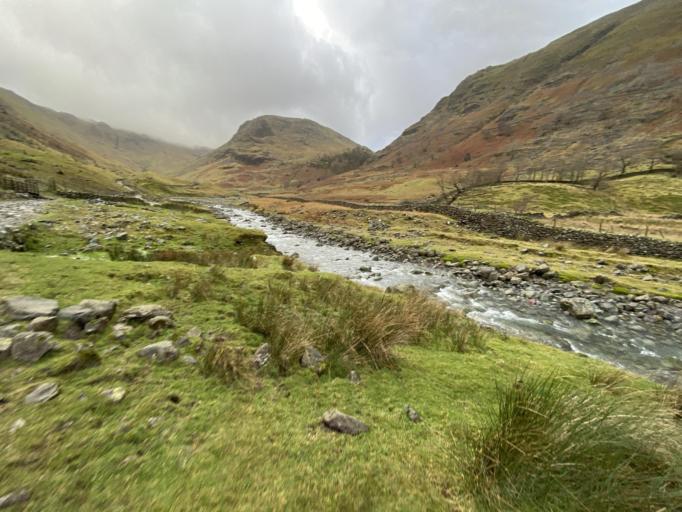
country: GB
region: England
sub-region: Cumbria
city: Keswick
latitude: 54.4941
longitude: -3.1825
